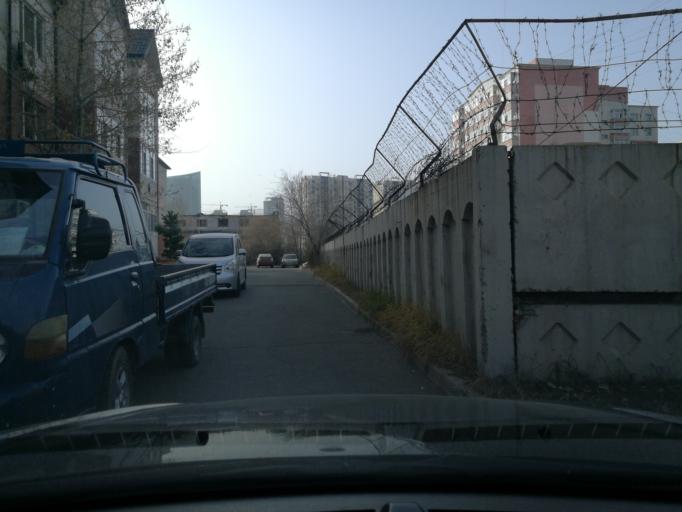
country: MN
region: Ulaanbaatar
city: Ulaanbaatar
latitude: 47.9101
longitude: 106.9097
